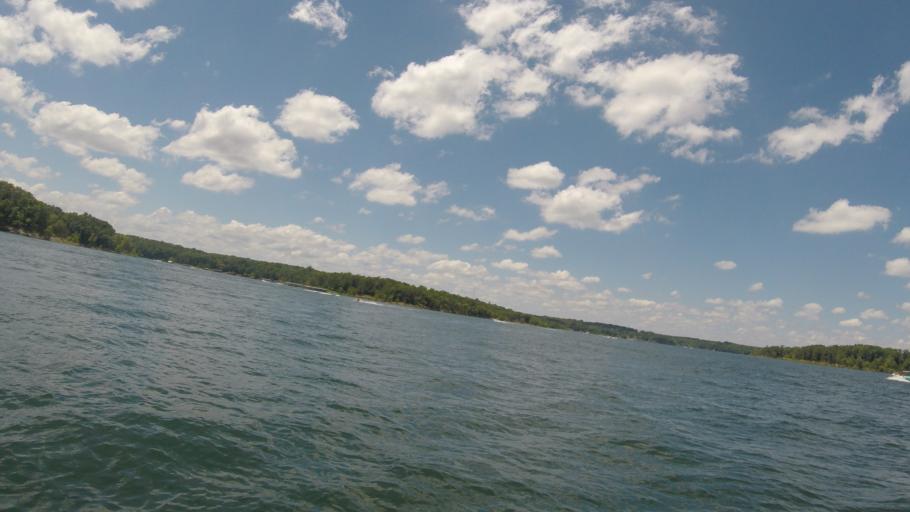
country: US
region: Missouri
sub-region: Barry County
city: Shell Knob
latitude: 36.5886
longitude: -93.5613
